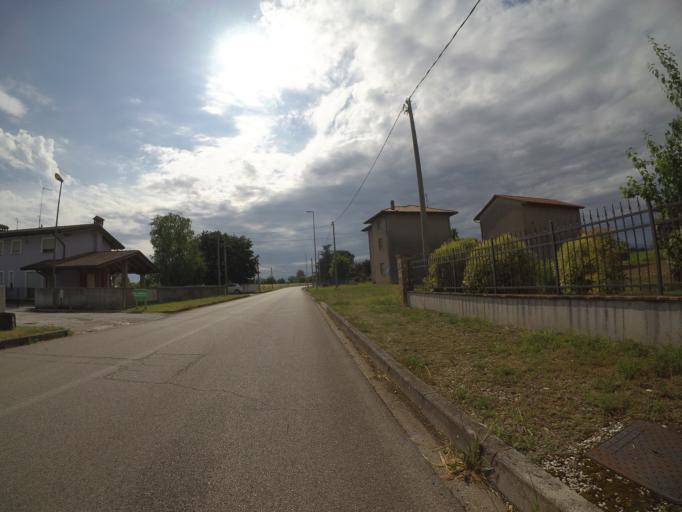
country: IT
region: Friuli Venezia Giulia
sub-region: Provincia di Udine
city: Lestizza
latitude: 45.9577
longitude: 13.1344
